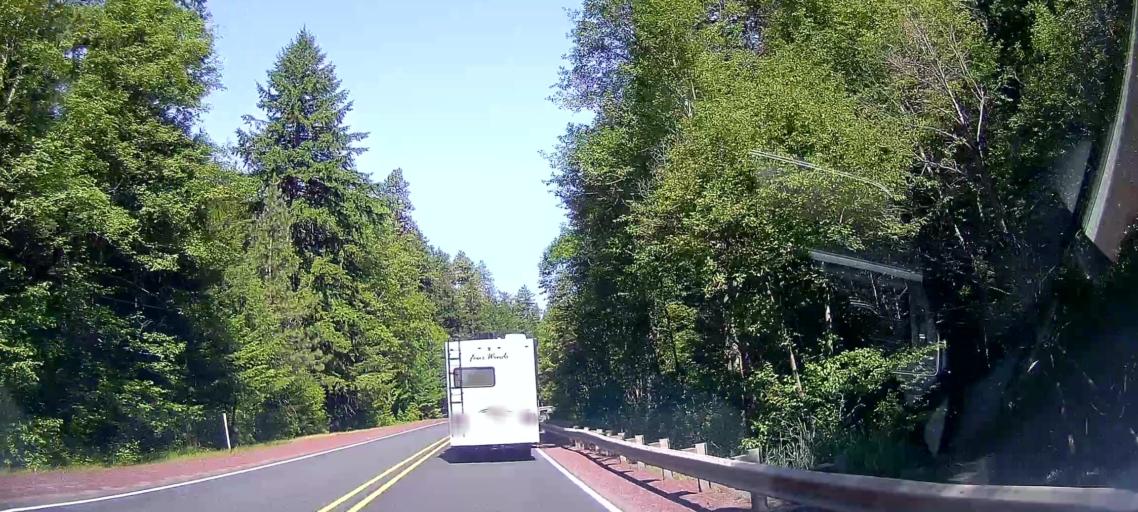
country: US
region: Oregon
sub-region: Jefferson County
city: Warm Springs
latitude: 45.0732
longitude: -121.5334
